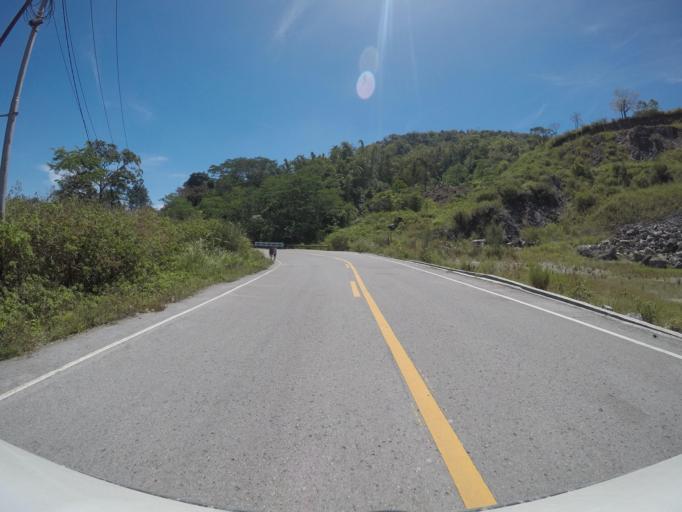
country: TL
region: Manatuto
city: Manatuto
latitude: -8.7873
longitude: 125.9690
